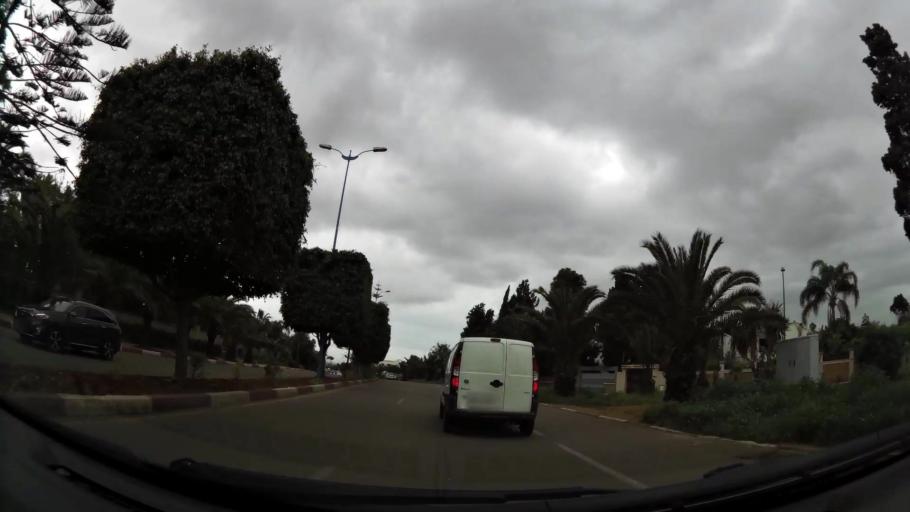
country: MA
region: Grand Casablanca
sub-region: Casablanca
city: Casablanca
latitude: 33.5341
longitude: -7.6296
